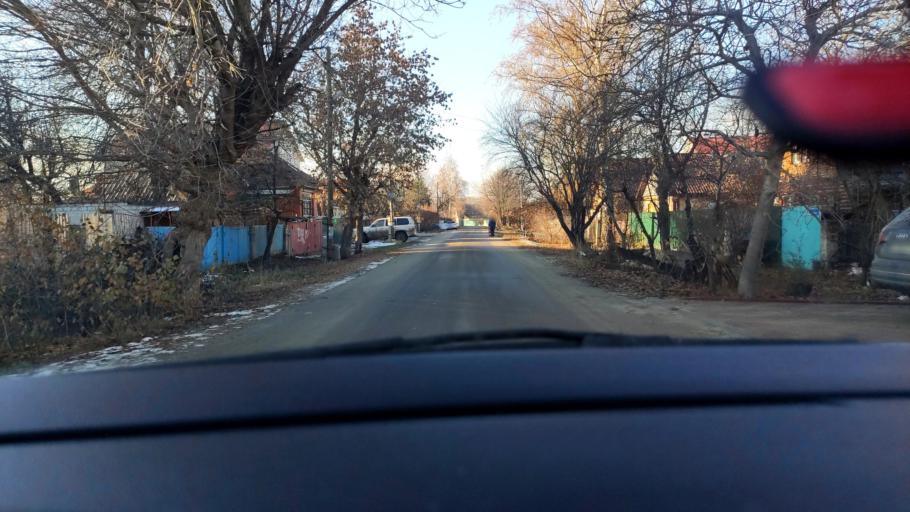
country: RU
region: Voronezj
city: Voronezh
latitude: 51.6315
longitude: 39.1788
